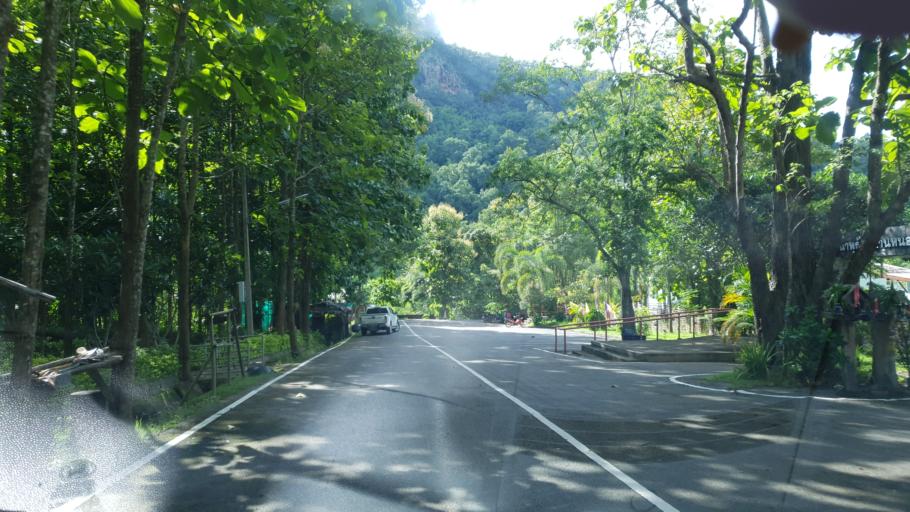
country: TH
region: Mae Hong Son
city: Khun Yuam
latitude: 18.6562
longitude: 97.9450
